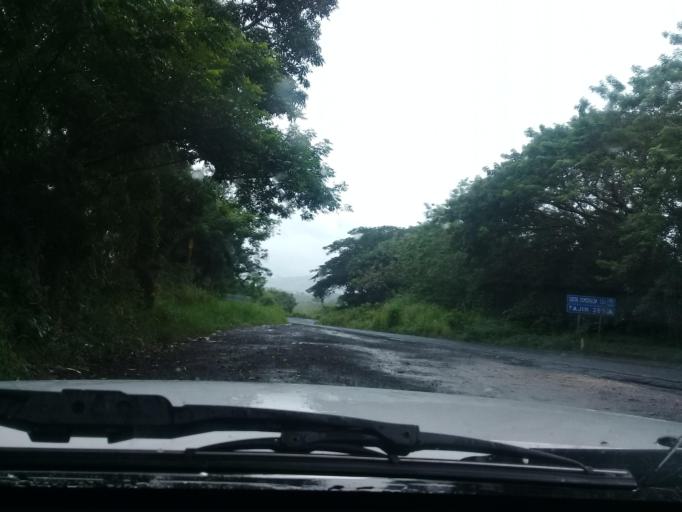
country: MX
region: Veracruz
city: Santiago Tuxtla
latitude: 18.4594
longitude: -95.2951
